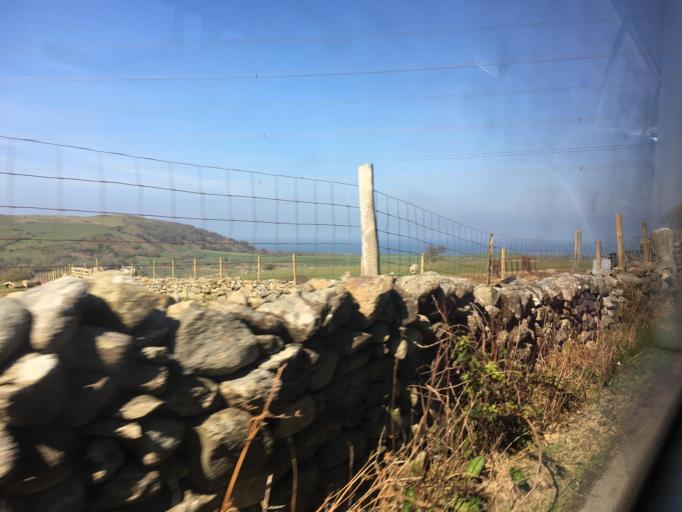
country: GB
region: Wales
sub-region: Gwynedd
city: Llanwnda
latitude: 53.0302
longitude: -4.2847
